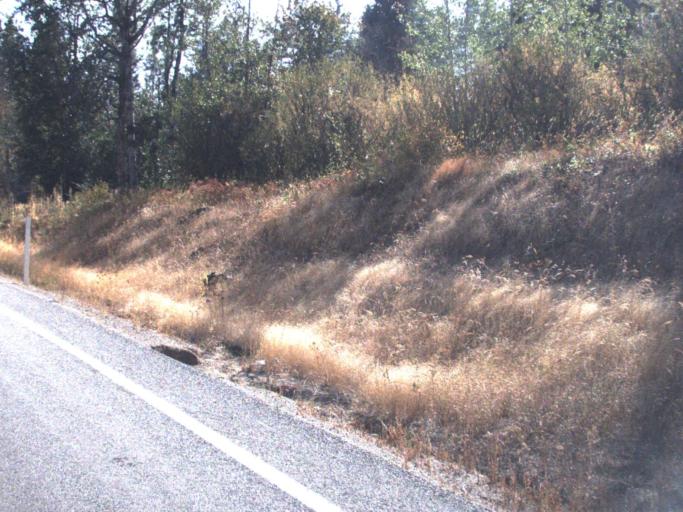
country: US
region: Washington
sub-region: Pend Oreille County
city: Newport
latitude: 48.1091
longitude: -117.2771
